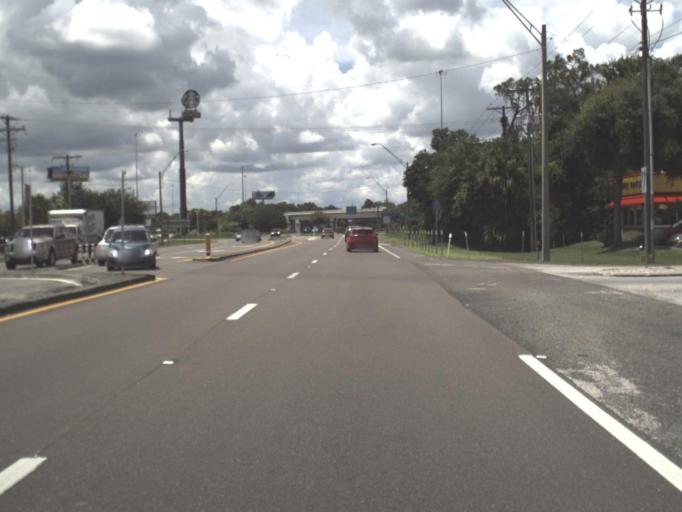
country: US
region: Florida
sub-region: Hillsborough County
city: Plant City
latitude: 28.0253
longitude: -82.1496
